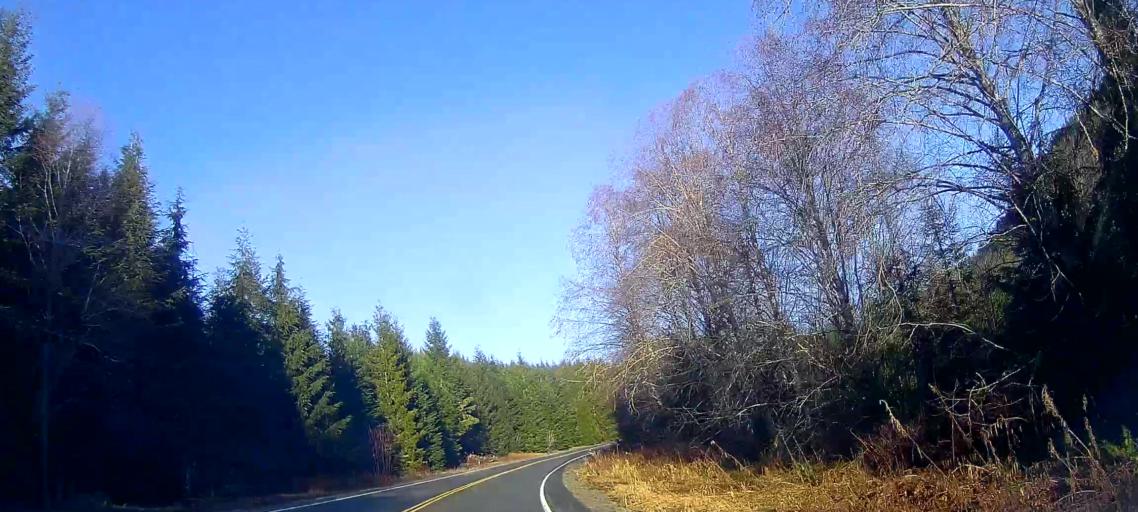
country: US
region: Washington
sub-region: Snohomish County
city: Darrington
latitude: 48.6353
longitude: -121.7400
